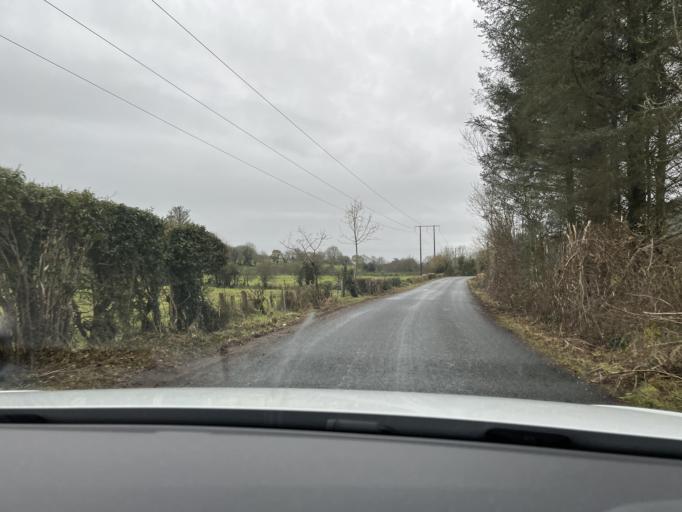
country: IE
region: Connaught
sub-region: County Leitrim
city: Manorhamilton
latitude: 54.2956
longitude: -8.1988
